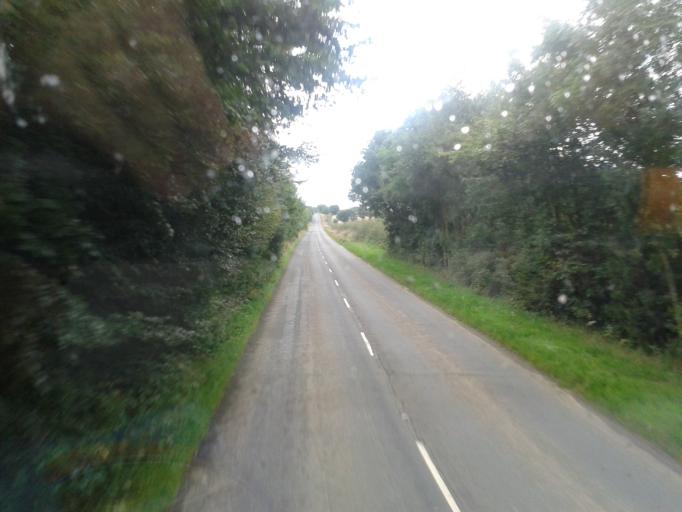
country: GB
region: England
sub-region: Devon
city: Okehampton
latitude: 50.7182
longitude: -3.8278
